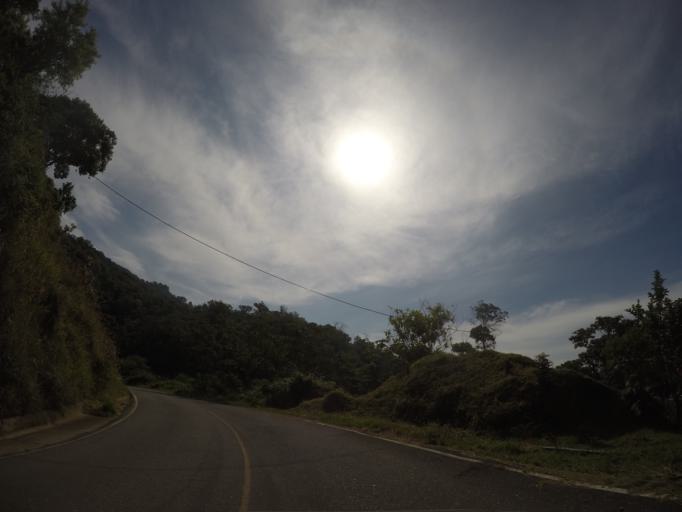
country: MX
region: Oaxaca
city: Pluma Hidalgo
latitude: 15.9309
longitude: -96.4217
